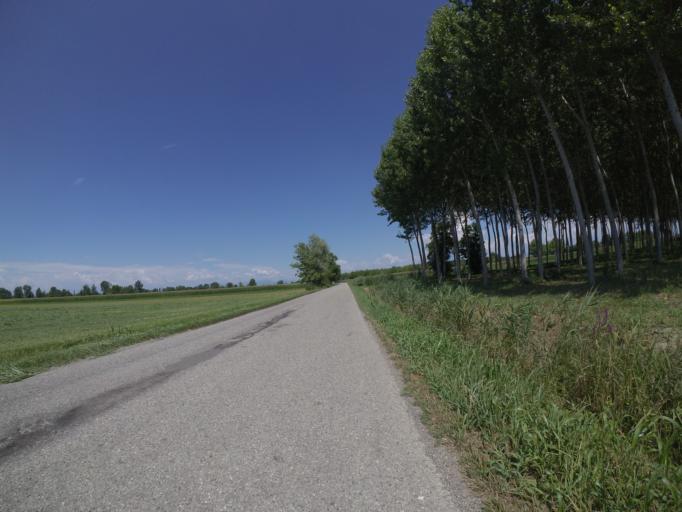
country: IT
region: Friuli Venezia Giulia
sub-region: Provincia di Udine
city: Talmassons
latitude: 45.9003
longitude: 13.1171
